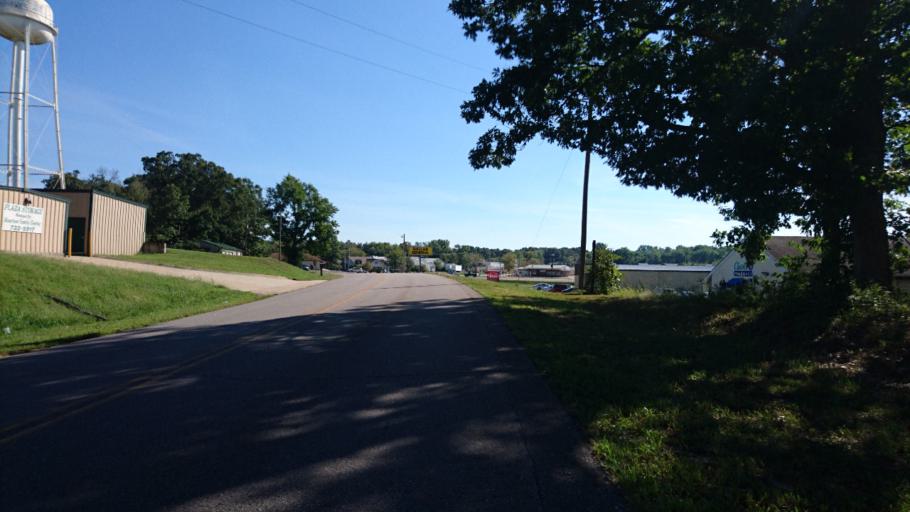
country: US
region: Missouri
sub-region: Crawford County
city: Bourbon
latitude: 38.1537
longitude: -91.2481
